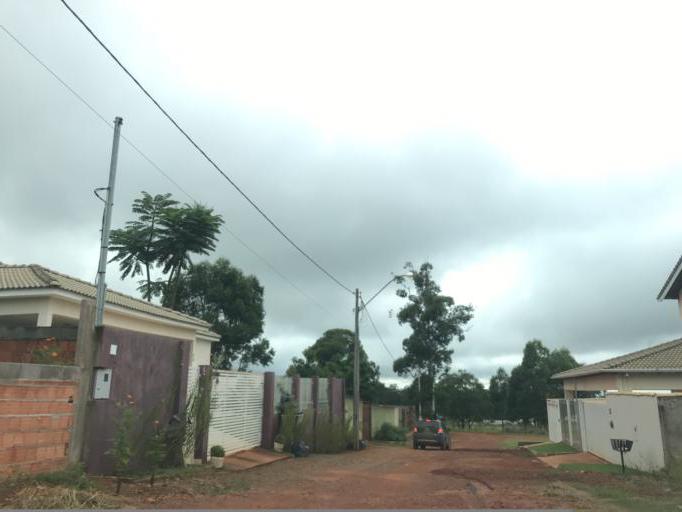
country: BR
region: Federal District
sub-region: Brasilia
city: Brasilia
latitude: -15.8306
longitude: -47.7940
